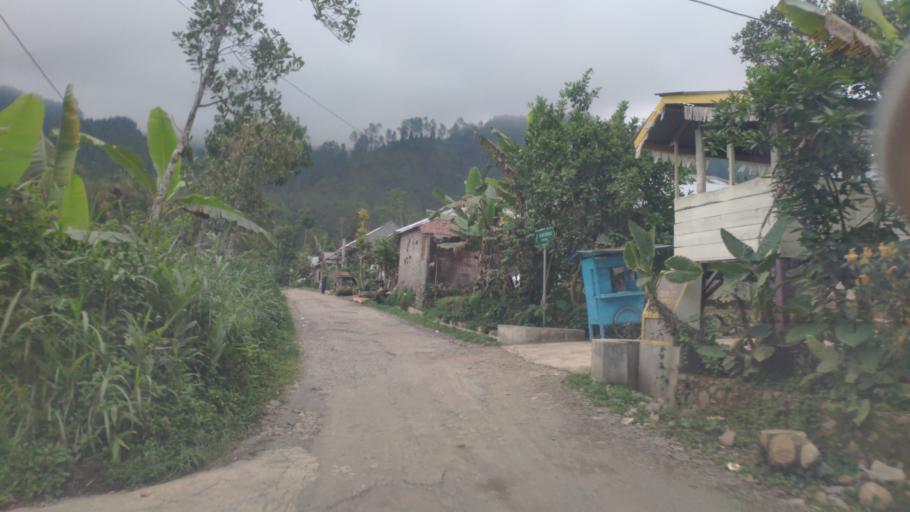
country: ID
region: Central Java
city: Wonosobo
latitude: -7.2353
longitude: 109.7413
